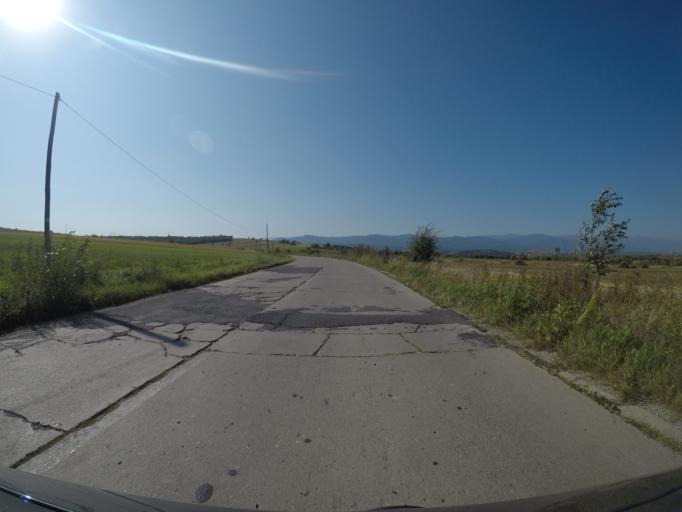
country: RO
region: Brasov
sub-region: Comuna Sinca Veche
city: Persani
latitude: 45.7808
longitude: 25.1916
